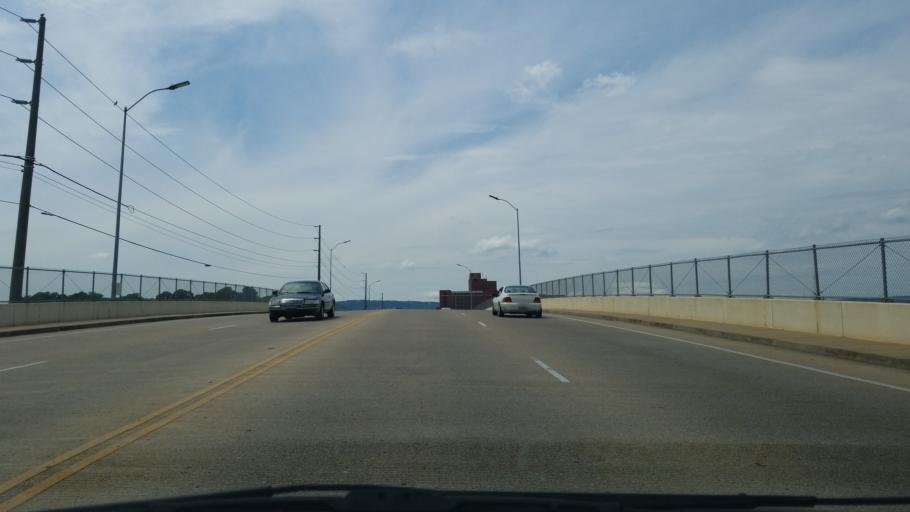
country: US
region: Tennessee
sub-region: Hamilton County
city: Chattanooga
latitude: 35.0446
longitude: -85.2819
